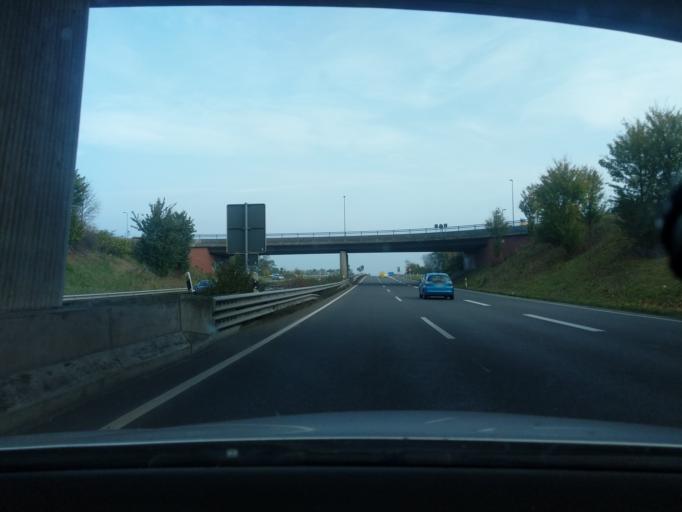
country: DE
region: Lower Saxony
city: Stade
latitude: 53.5816
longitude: 9.5007
